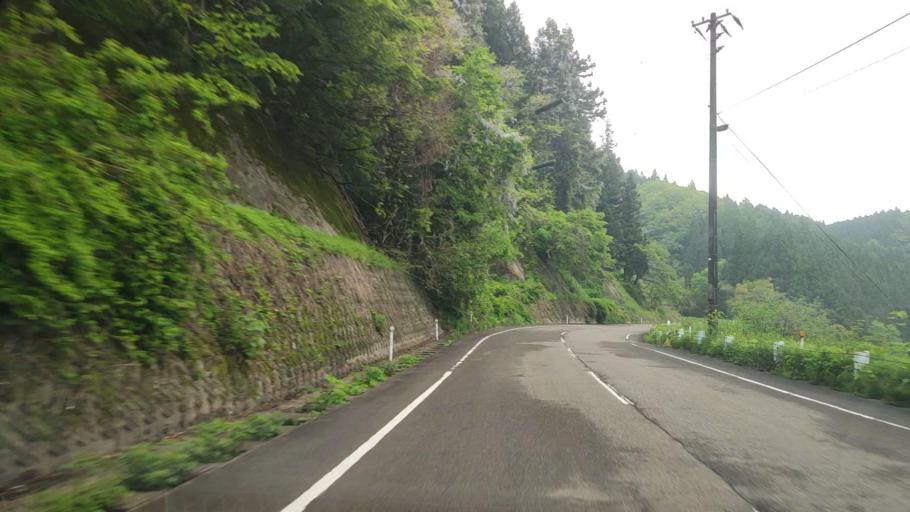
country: JP
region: Niigata
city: Gosen
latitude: 37.7143
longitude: 139.1121
